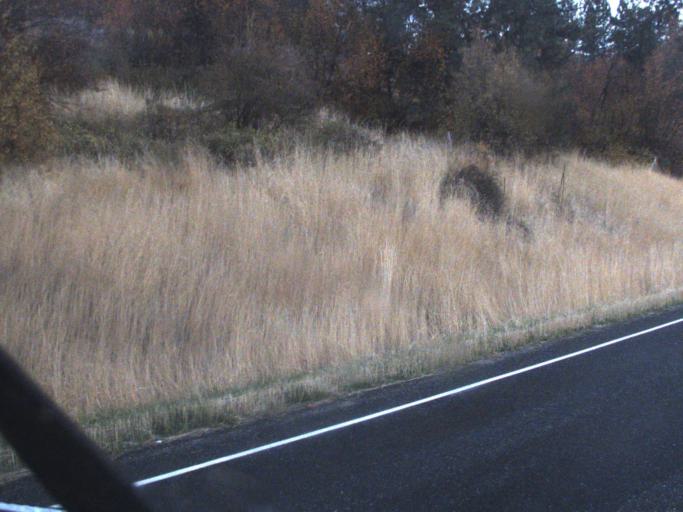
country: US
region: Washington
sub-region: Stevens County
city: Kettle Falls
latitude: 48.4577
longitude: -118.1791
